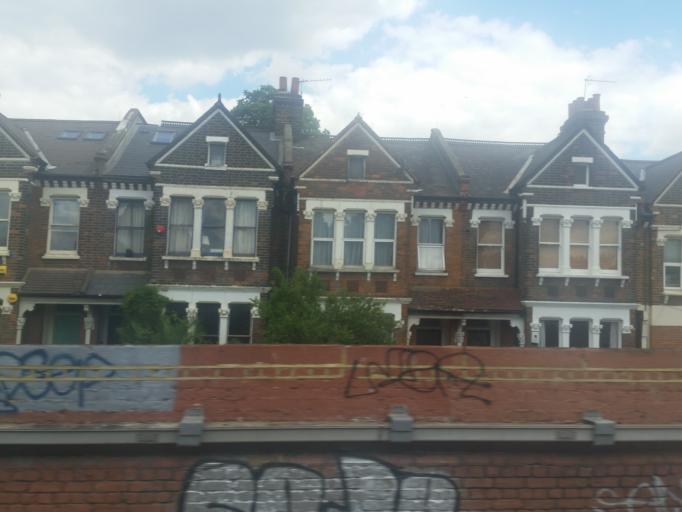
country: GB
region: England
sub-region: Greater London
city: Brixton
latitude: 51.4540
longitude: -0.1024
